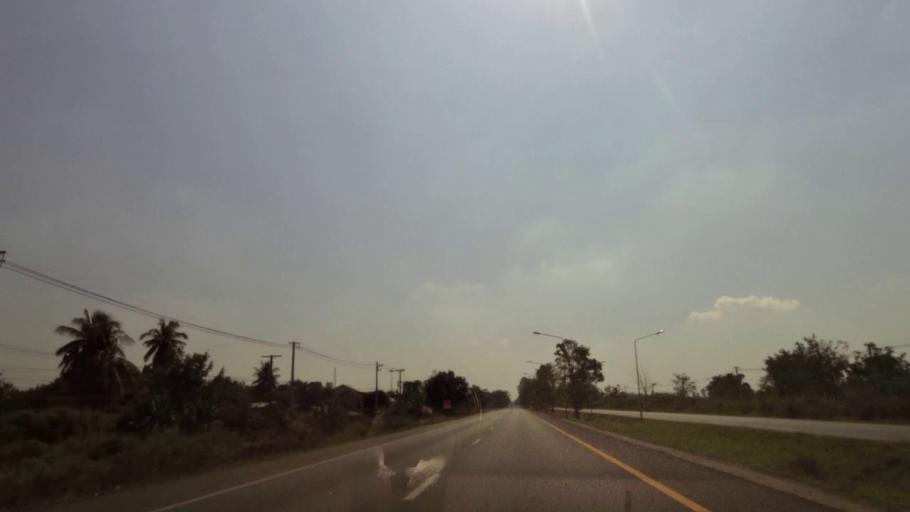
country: TH
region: Phichit
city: Bueng Na Rang
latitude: 16.2586
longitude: 100.1259
